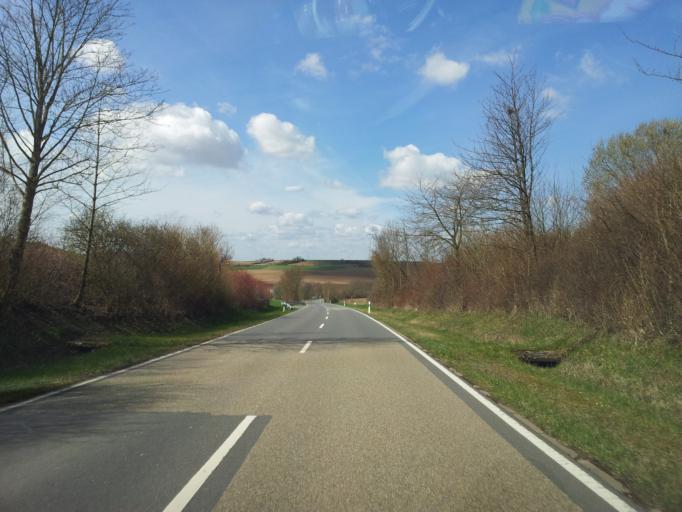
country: DE
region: Baden-Wuerttemberg
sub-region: Regierungsbezirk Stuttgart
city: Grossrinderfeld
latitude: 49.6971
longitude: 9.7857
